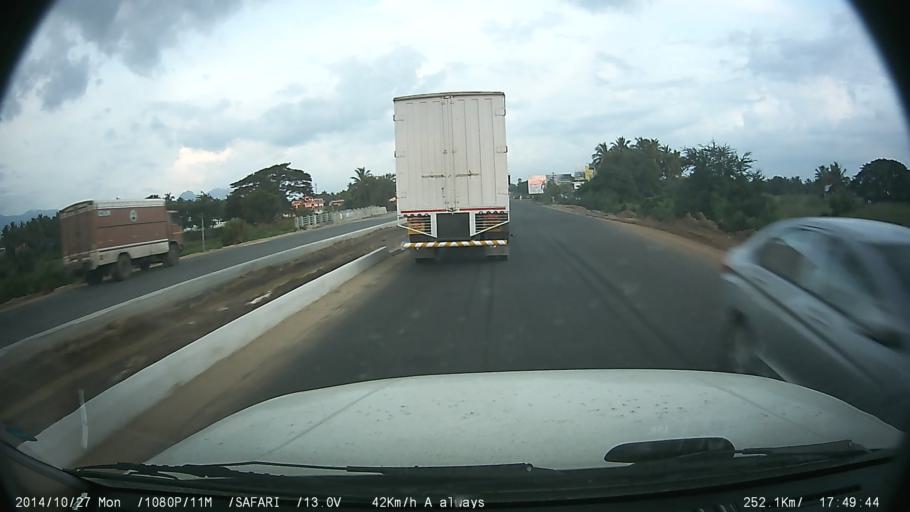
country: IN
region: Kerala
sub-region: Palakkad district
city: Palakkad
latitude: 10.7395
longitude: 76.6446
